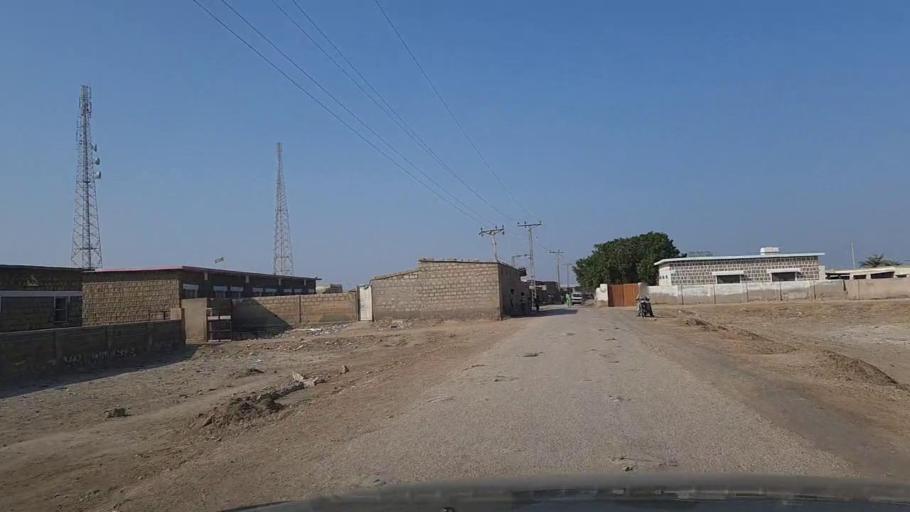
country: PK
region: Sindh
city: Keti Bandar
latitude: 24.1421
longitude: 67.4511
